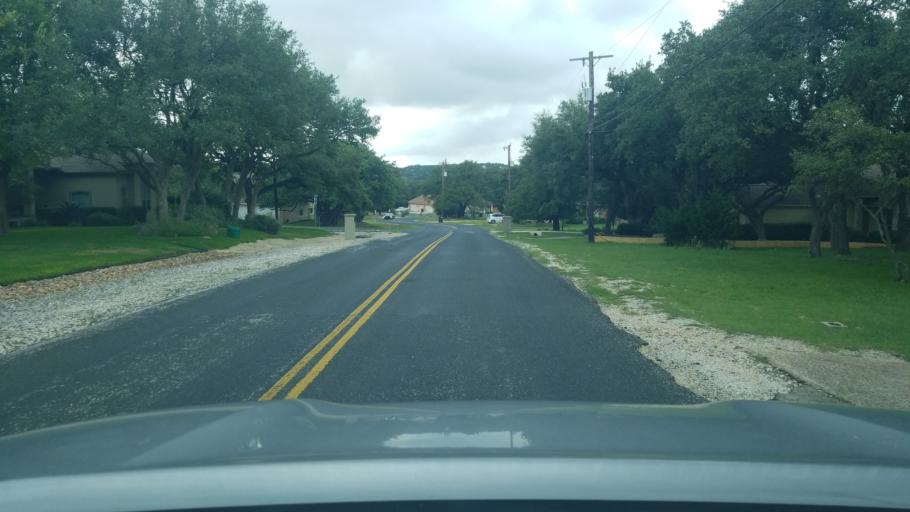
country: US
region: Texas
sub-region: Bexar County
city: Timberwood Park
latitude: 29.6949
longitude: -98.5016
